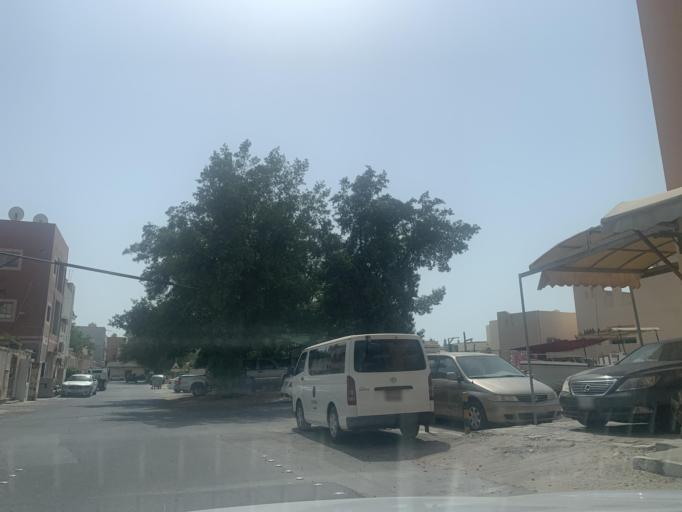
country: BH
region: Manama
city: Jidd Hafs
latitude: 26.2171
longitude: 50.4697
